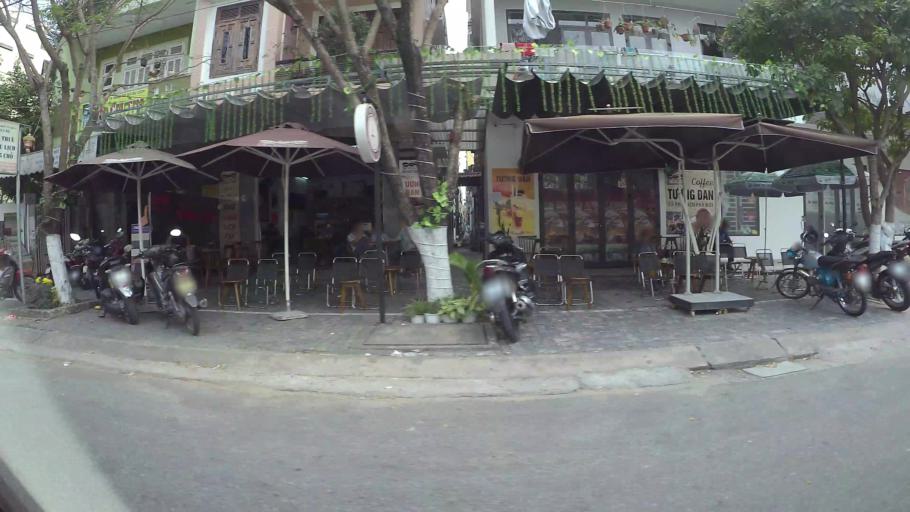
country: VN
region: Da Nang
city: Da Nang
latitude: 16.0440
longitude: 108.2104
